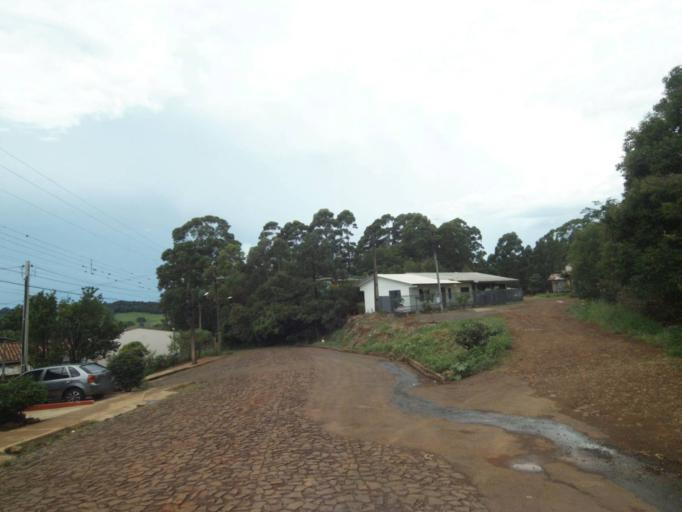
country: BR
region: Parana
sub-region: Guaraniacu
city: Guaraniacu
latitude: -25.0959
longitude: -52.8674
